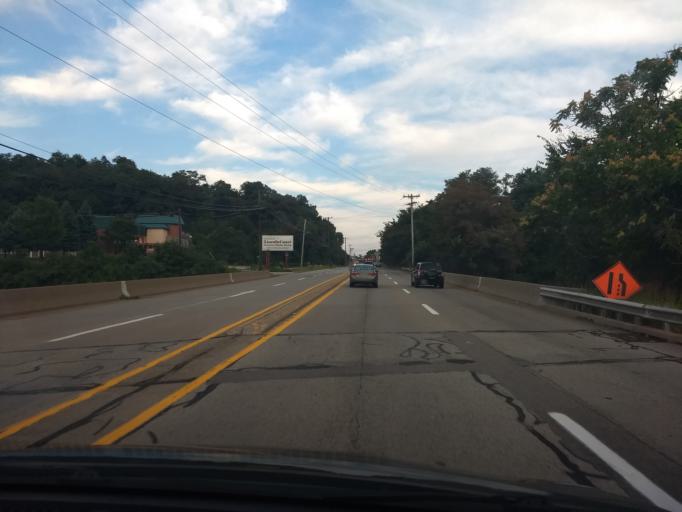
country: US
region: Pennsylvania
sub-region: Allegheny County
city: East Pittsburgh
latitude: 40.3878
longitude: -79.8289
